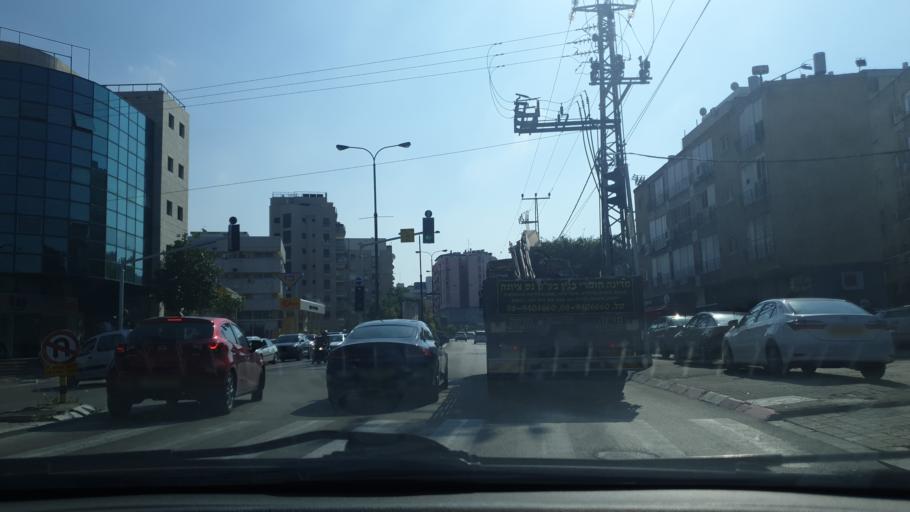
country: IL
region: Central District
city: Rishon LeZiyyon
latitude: 31.9727
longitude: 34.8065
